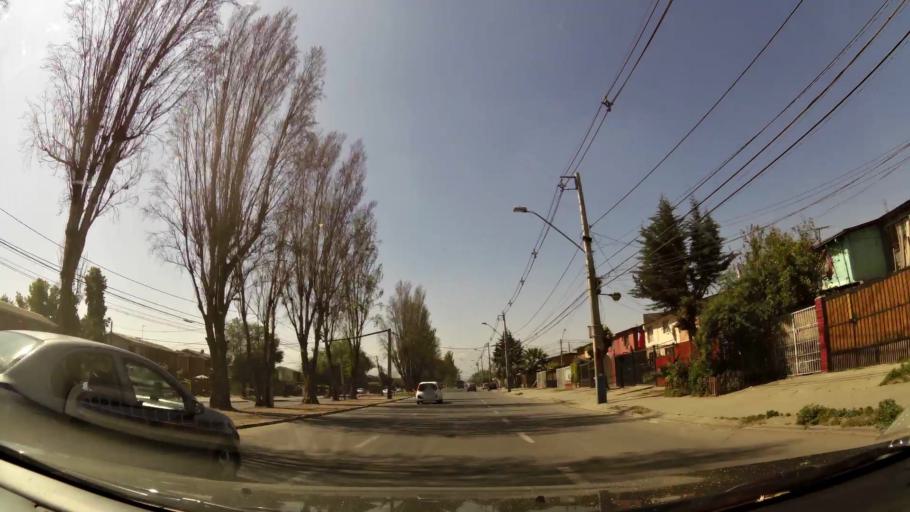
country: CL
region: Santiago Metropolitan
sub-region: Provincia de Santiago
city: Lo Prado
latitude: -33.3613
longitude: -70.7510
